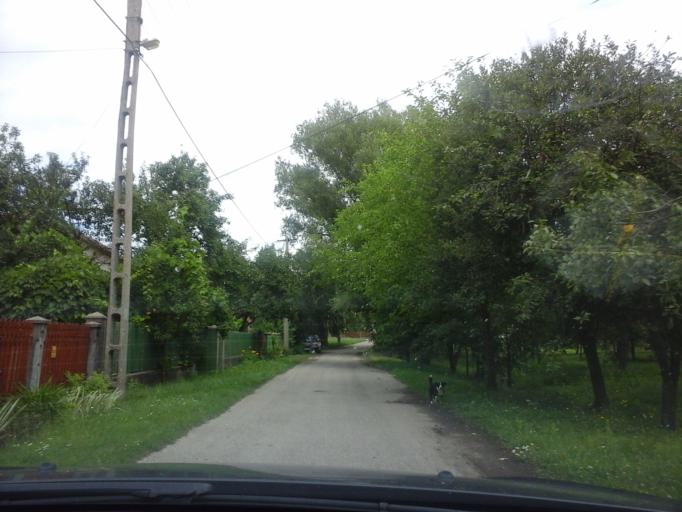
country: HU
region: Borsod-Abauj-Zemplen
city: Sajokaza
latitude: 48.3313
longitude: 20.5959
